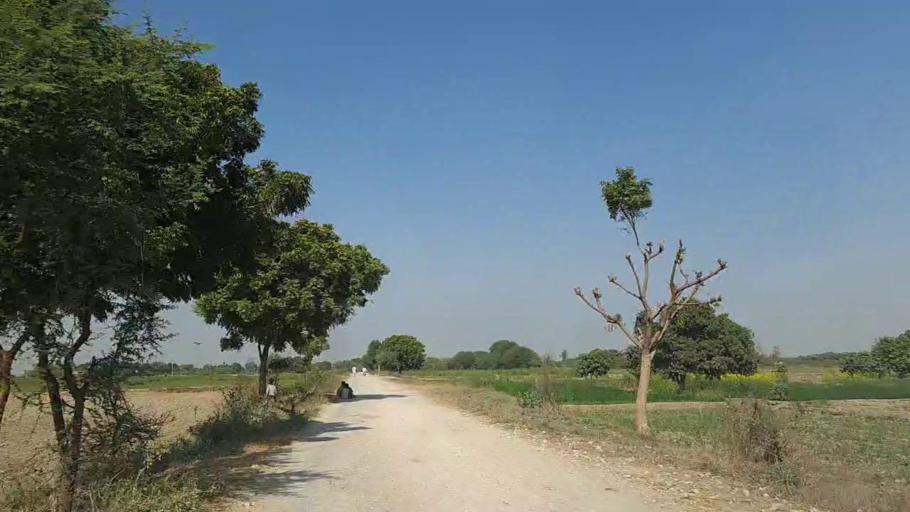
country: PK
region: Sindh
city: Naukot
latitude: 24.8693
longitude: 69.4037
